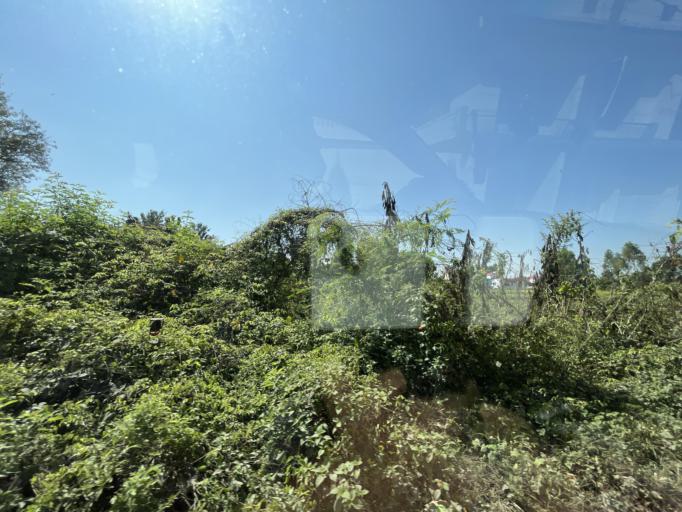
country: IN
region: Uttarakhand
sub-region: Naini Tal
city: Haldwani
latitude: 29.2136
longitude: 79.4548
